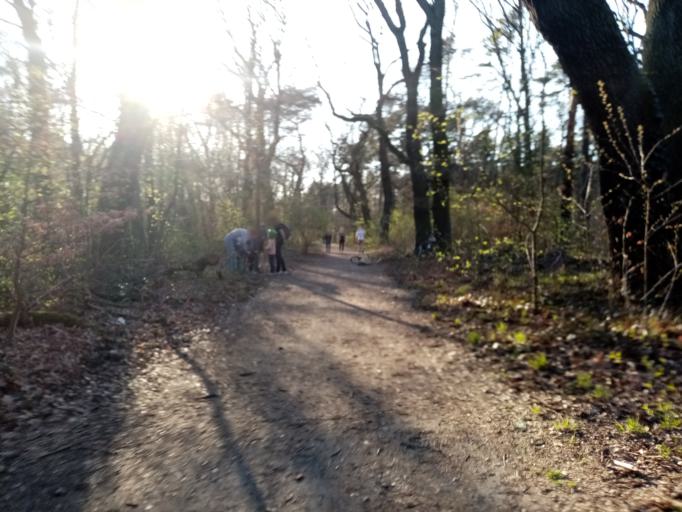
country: DE
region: Berlin
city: Karlshorst
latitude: 52.4663
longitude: 13.5410
